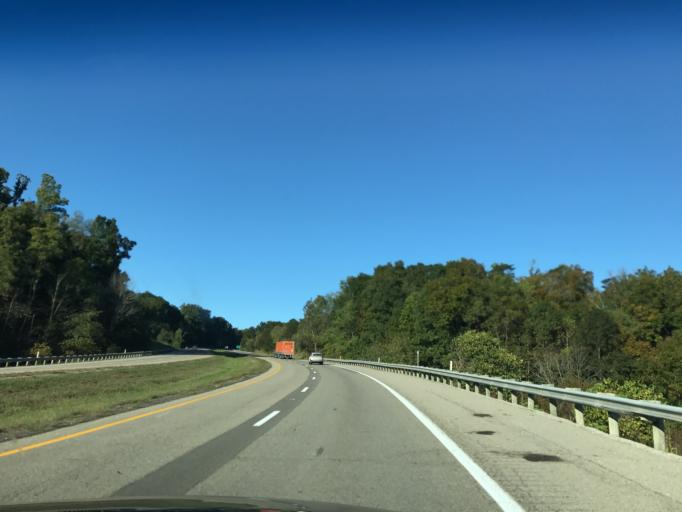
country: US
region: Ohio
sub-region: Washington County
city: Newport
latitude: 39.2530
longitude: -81.2515
